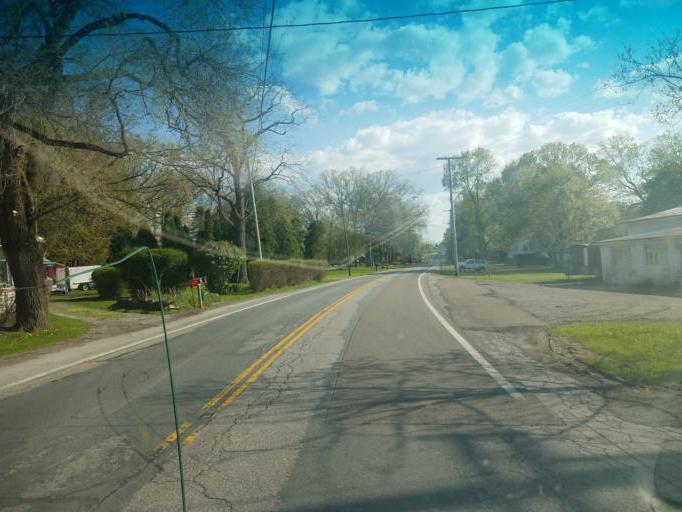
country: US
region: Ohio
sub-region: Wayne County
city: Shreve
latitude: 40.7116
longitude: -81.9451
